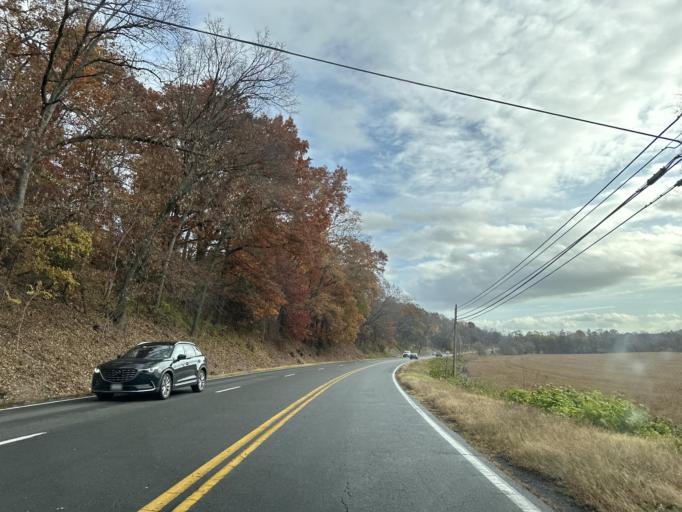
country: US
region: Virginia
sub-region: Shenandoah County
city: Strasburg
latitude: 38.9881
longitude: -78.3793
